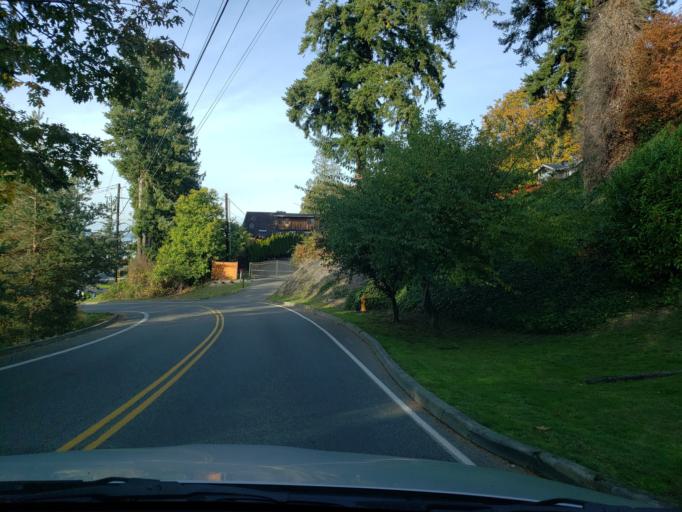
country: US
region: Washington
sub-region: Snohomish County
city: Mukilteo
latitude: 47.9399
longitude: -122.3038
